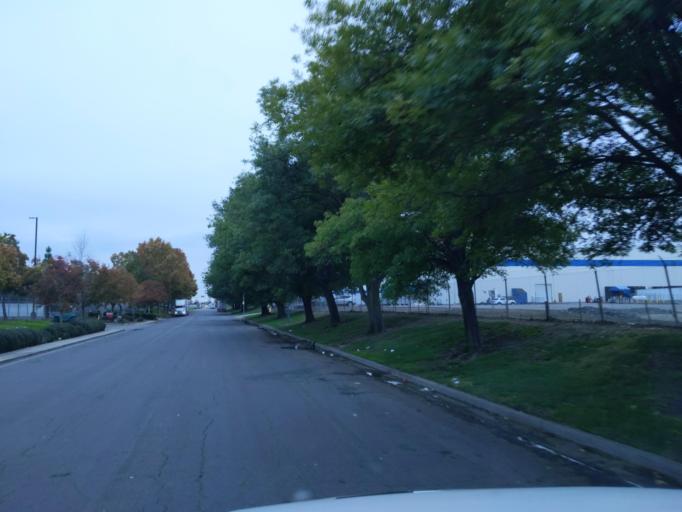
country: US
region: California
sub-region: San Joaquin County
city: Taft Mosswood
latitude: 37.9159
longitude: -121.2690
